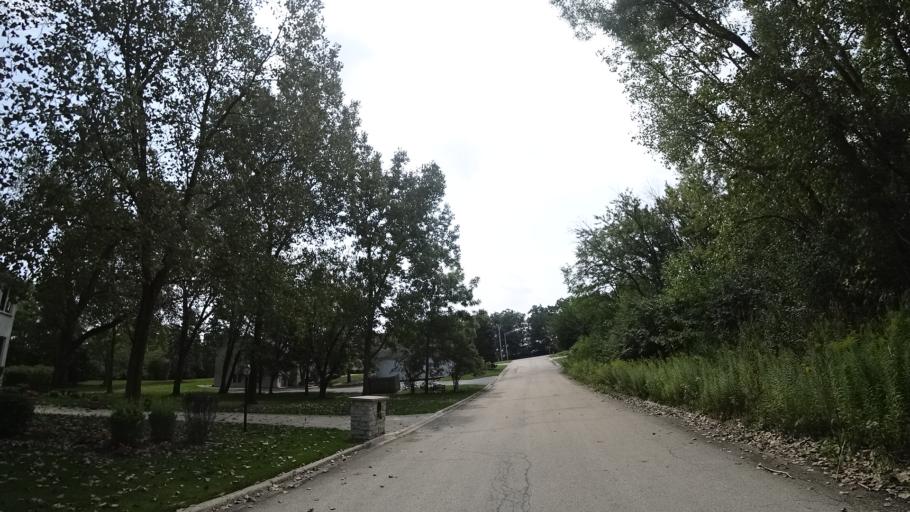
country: US
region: Illinois
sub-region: Cook County
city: Orland Park
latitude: 41.6309
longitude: -87.8789
